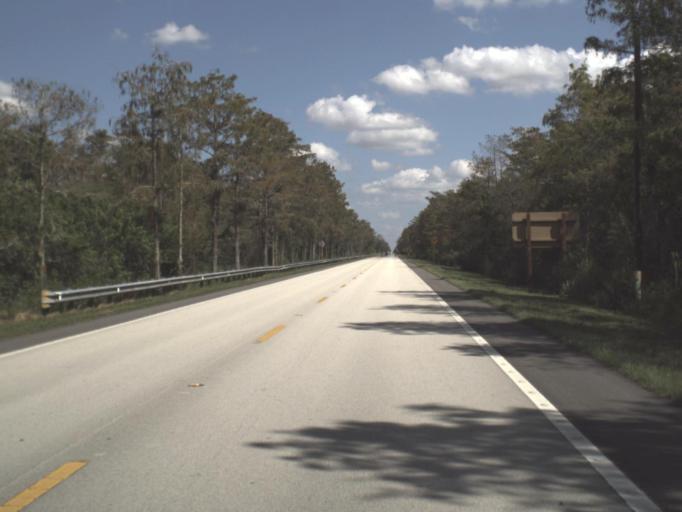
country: US
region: Florida
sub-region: Miami-Dade County
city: Kendall West
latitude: 25.8564
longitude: -81.0287
